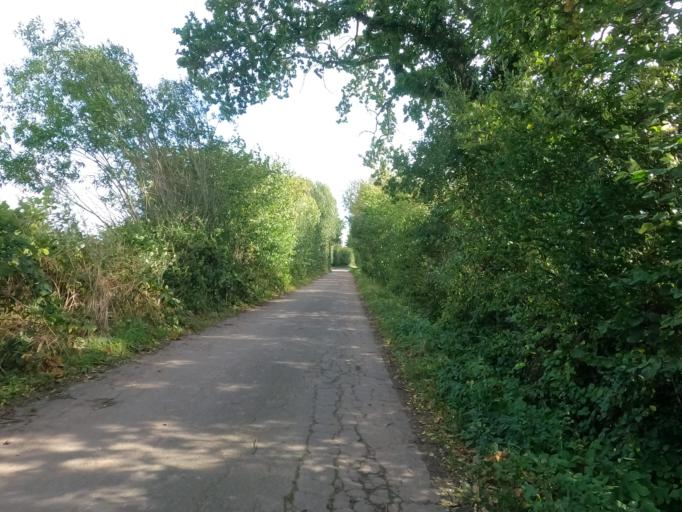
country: DE
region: Schleswig-Holstein
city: Riepsdorf
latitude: 54.2306
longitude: 10.9876
